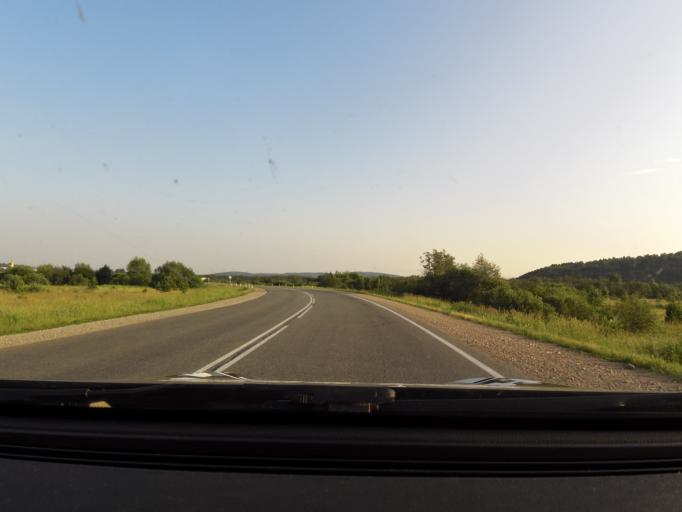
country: RU
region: Sverdlovsk
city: Mikhaylovsk
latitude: 56.4501
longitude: 59.0841
